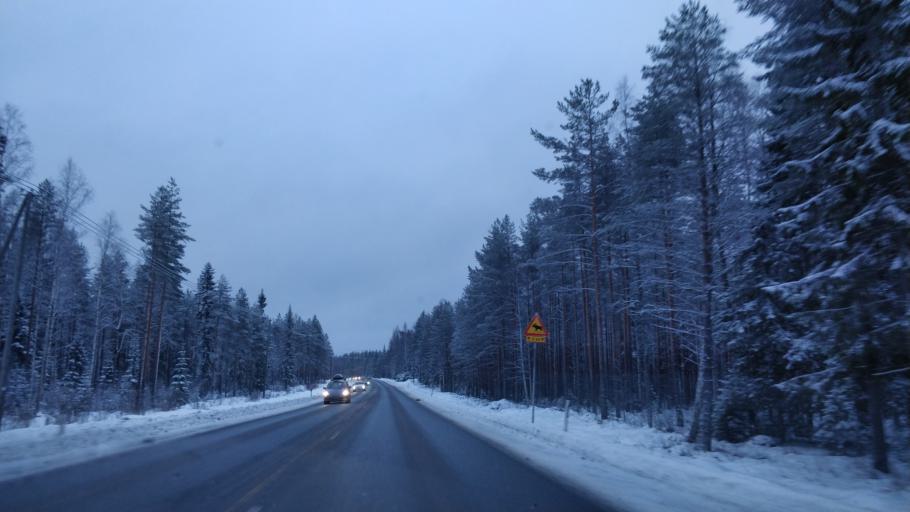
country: FI
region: Central Finland
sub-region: Saarijaervi-Viitasaari
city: Pihtipudas
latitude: 63.2126
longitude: 25.6766
